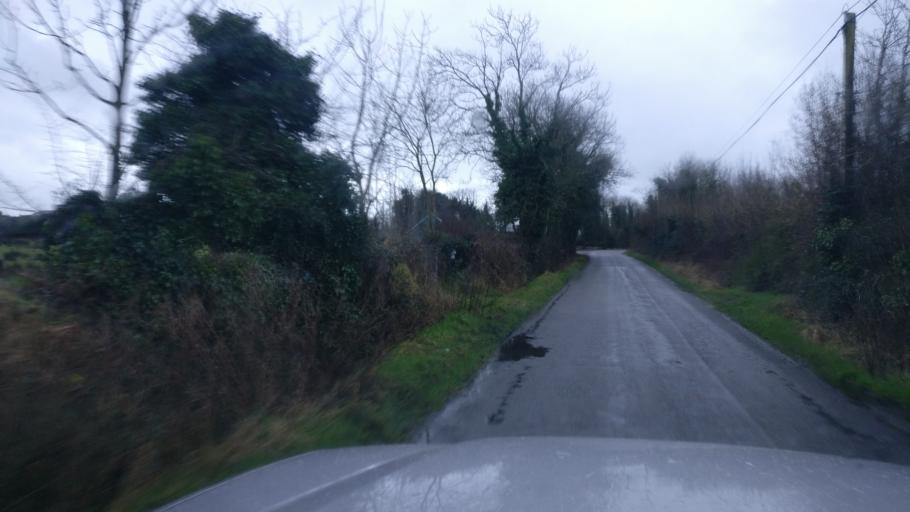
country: IE
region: Connaught
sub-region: County Galway
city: Ballinasloe
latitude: 53.2770
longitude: -8.3406
